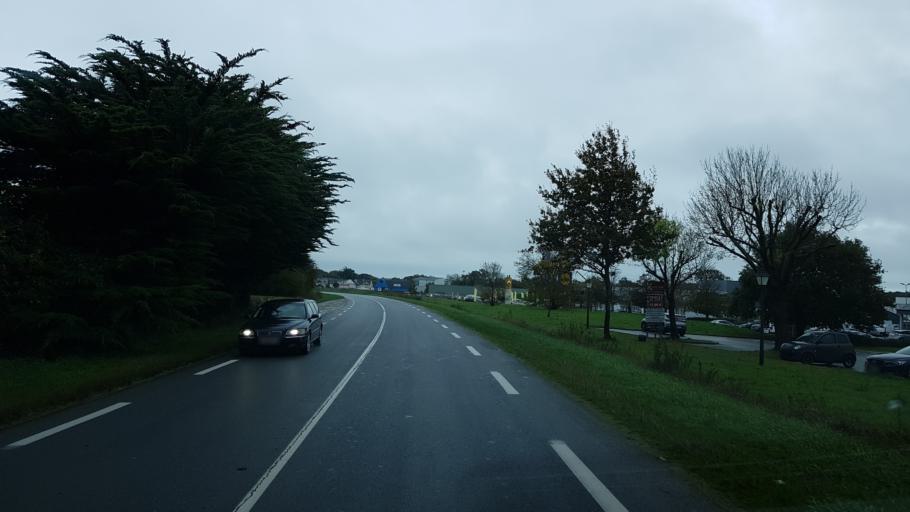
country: FR
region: Brittany
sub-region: Departement du Morbihan
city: Sarzeau
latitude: 47.5228
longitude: -2.7845
